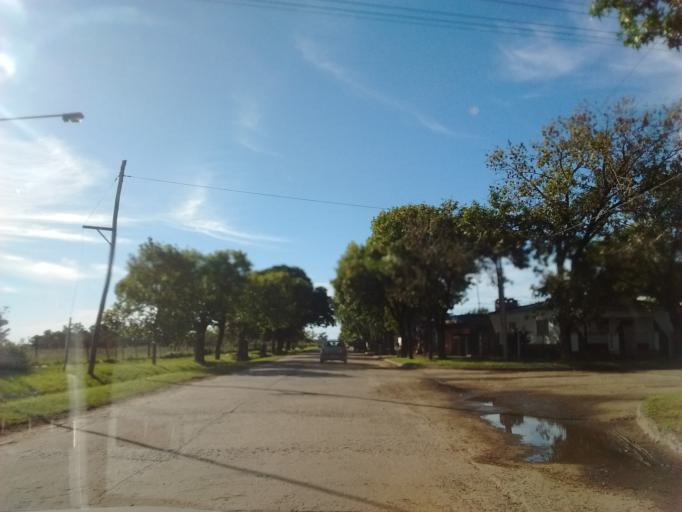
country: AR
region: Santa Fe
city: Coronda
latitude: -32.2285
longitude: -60.9780
